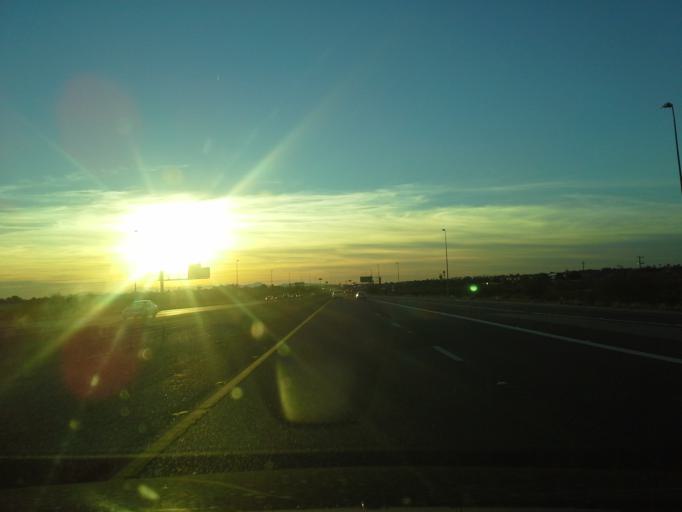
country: US
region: Arizona
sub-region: Pinal County
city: Apache Junction
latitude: 33.3869
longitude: -111.5158
